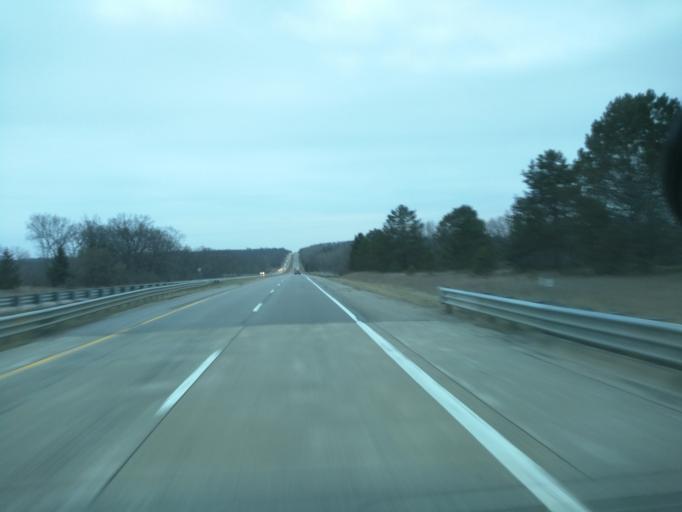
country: US
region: Michigan
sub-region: Ingham County
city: Leslie
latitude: 42.4114
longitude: -84.4293
